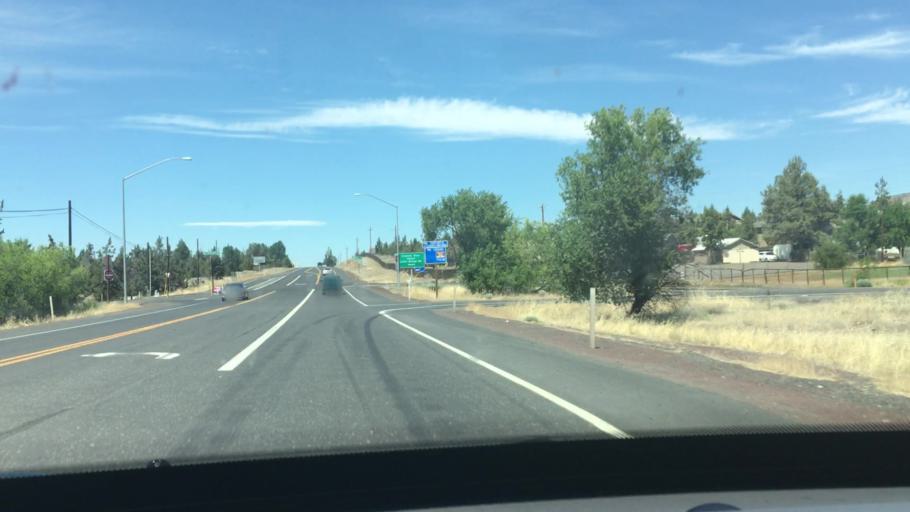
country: US
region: Oregon
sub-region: Deschutes County
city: Terrebonne
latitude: 44.3585
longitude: -121.1786
